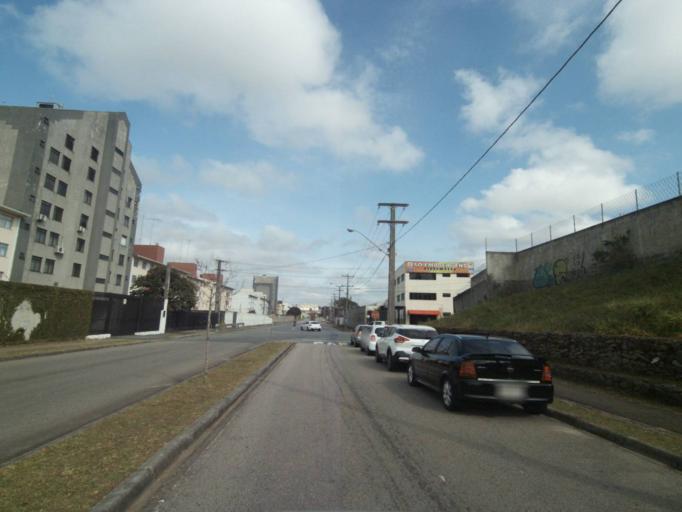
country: BR
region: Parana
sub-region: Curitiba
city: Curitiba
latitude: -25.4668
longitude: -49.2562
